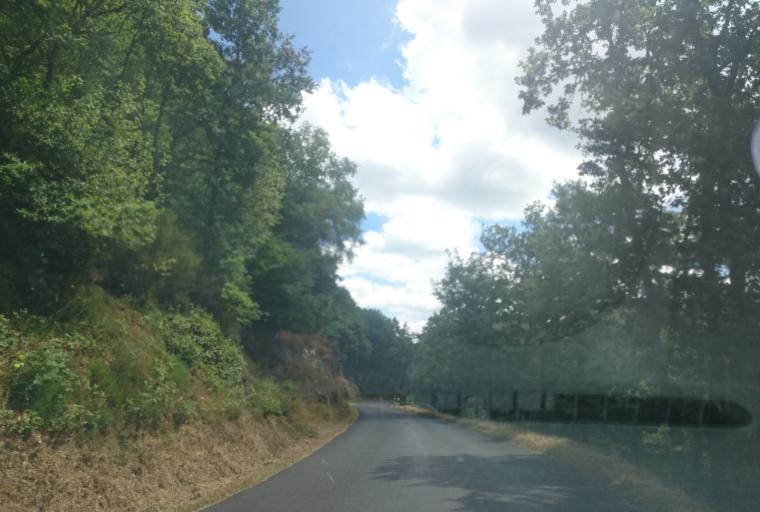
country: FR
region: Auvergne
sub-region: Departement du Cantal
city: Laroquebrou
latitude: 44.9781
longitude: 2.1640
